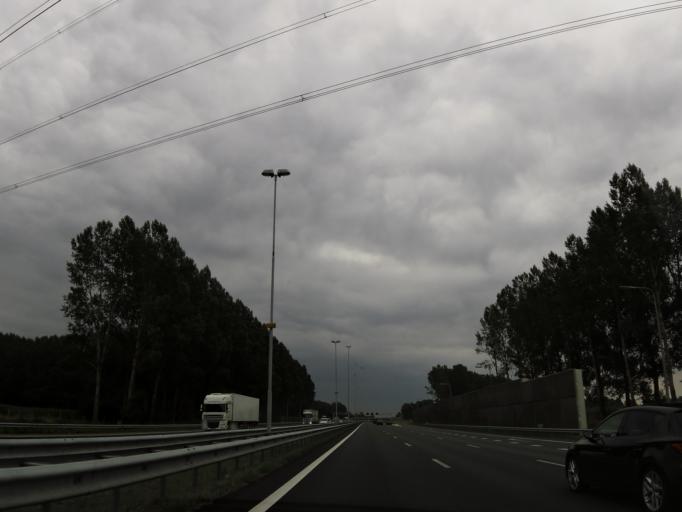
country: NL
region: North Brabant
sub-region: Gemeente Best
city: Best
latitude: 51.5277
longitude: 5.3889
